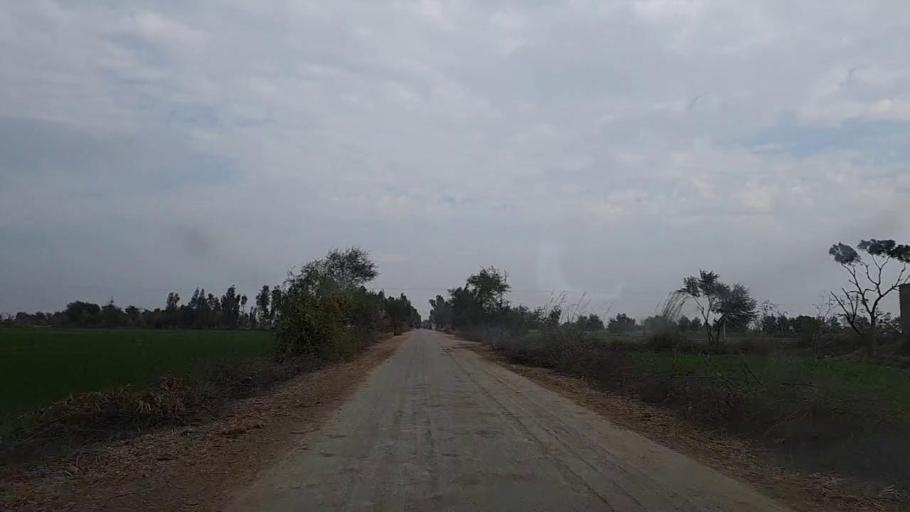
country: PK
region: Sindh
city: Sanghar
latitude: 26.2291
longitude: 69.0169
